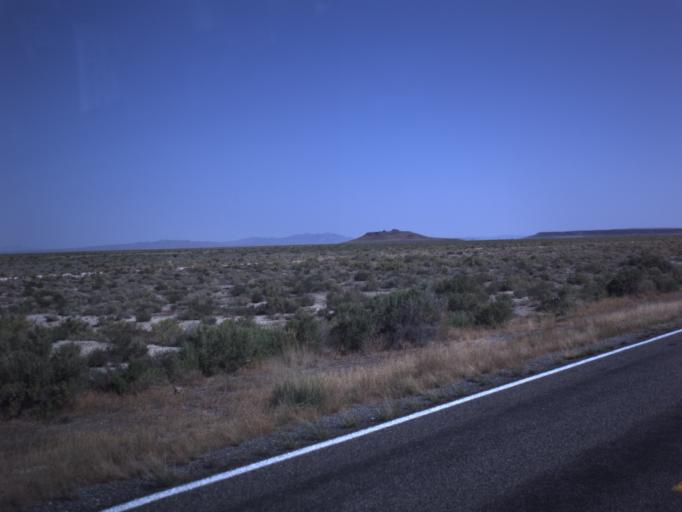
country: US
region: Utah
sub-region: Millard County
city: Delta
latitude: 39.0810
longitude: -112.7552
